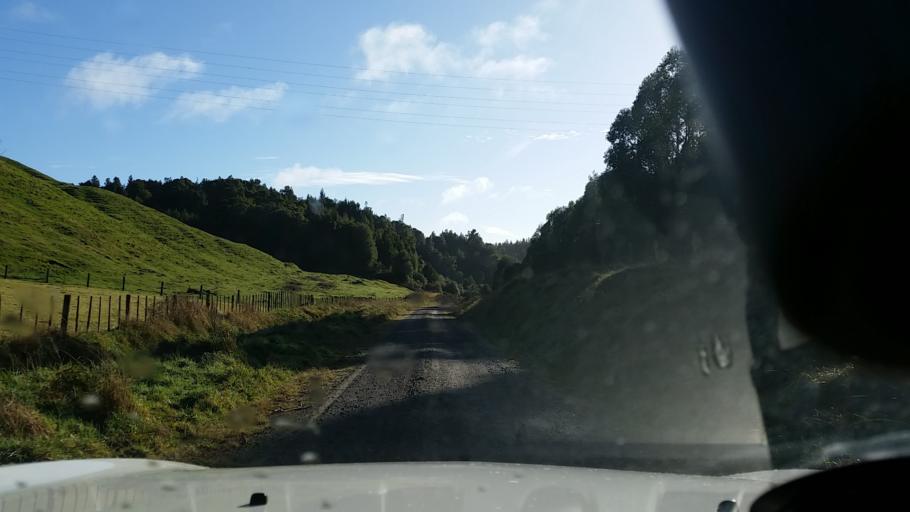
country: NZ
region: Bay of Plenty
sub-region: Kawerau District
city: Kawerau
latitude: -38.0122
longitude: 176.5973
